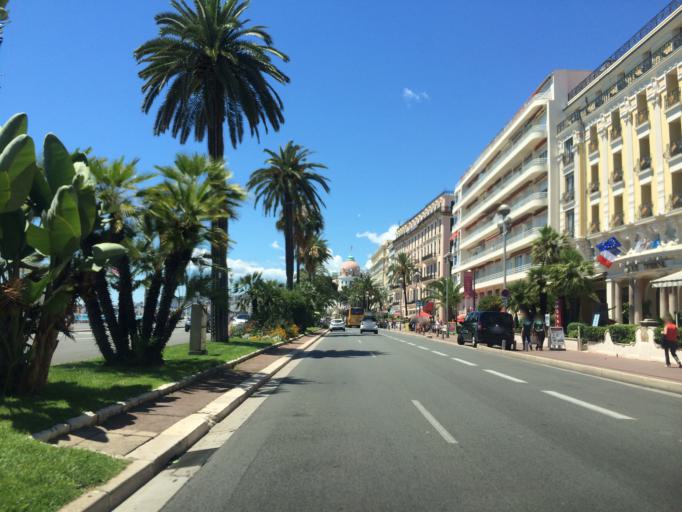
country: FR
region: Provence-Alpes-Cote d'Azur
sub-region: Departement des Alpes-Maritimes
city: Nice
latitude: 43.6948
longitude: 7.2625
